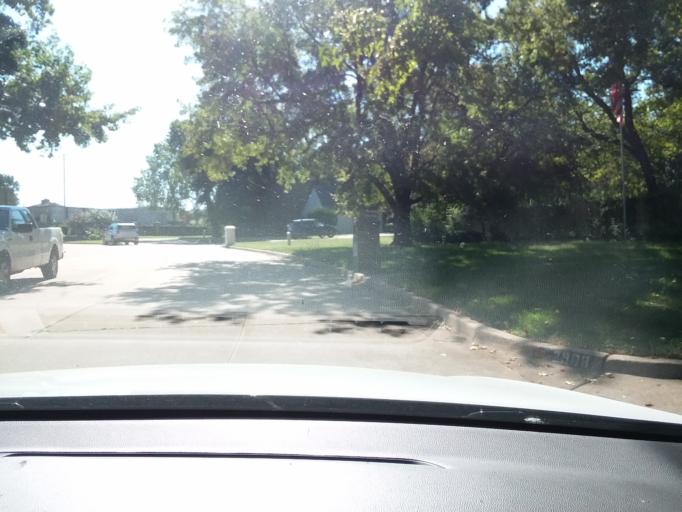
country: US
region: Oklahoma
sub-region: Oklahoma County
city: The Village
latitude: 35.5994
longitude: -97.5682
